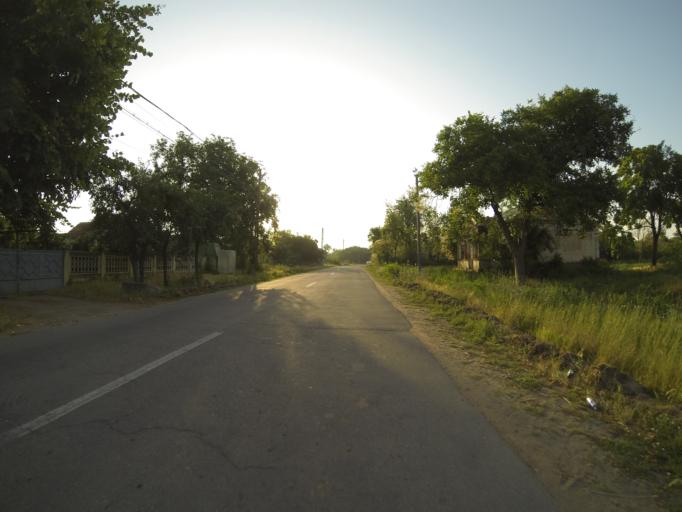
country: RO
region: Dolj
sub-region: Comuna Dobrotesti
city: Dobrotesti
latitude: 43.9599
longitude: 24.1273
